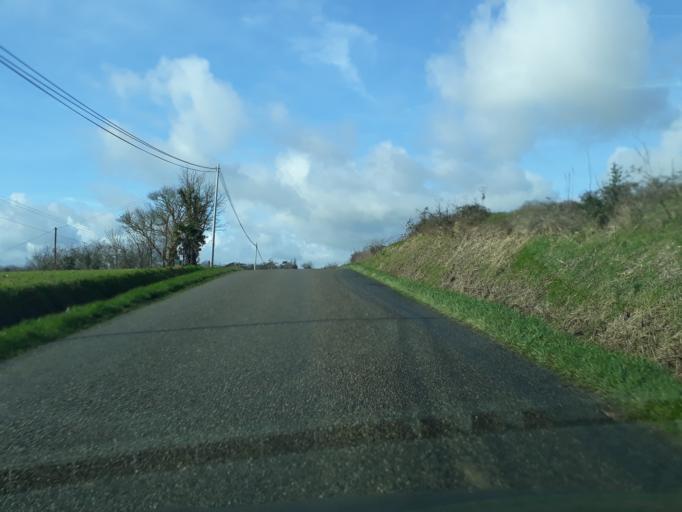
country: FR
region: Midi-Pyrenees
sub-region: Departement du Gers
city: Pujaudran
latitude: 43.6190
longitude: 1.0418
